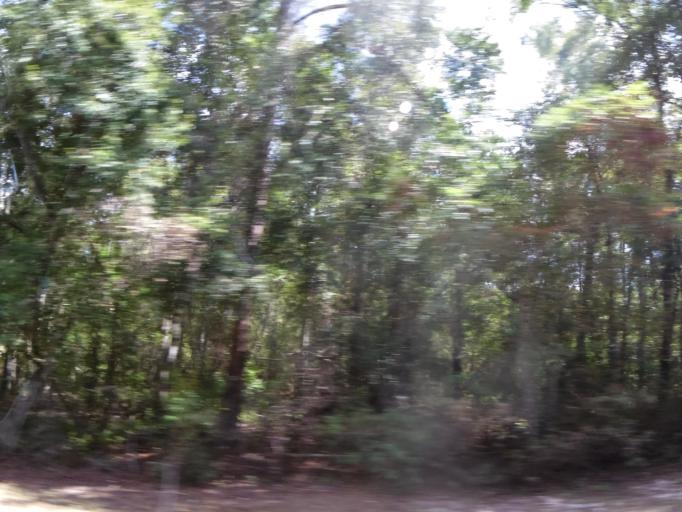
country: US
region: Georgia
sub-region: Charlton County
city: Folkston
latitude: 31.0153
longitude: -82.0252
